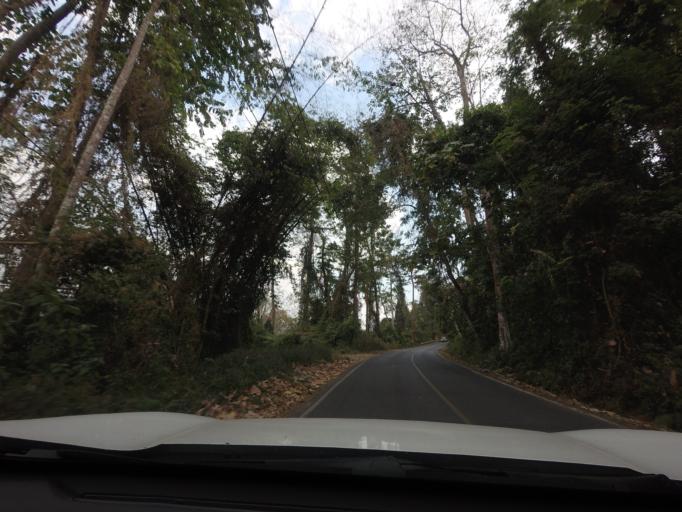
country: TH
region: Nakhon Ratchasima
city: Pak Chong
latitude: 14.4788
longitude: 101.3873
